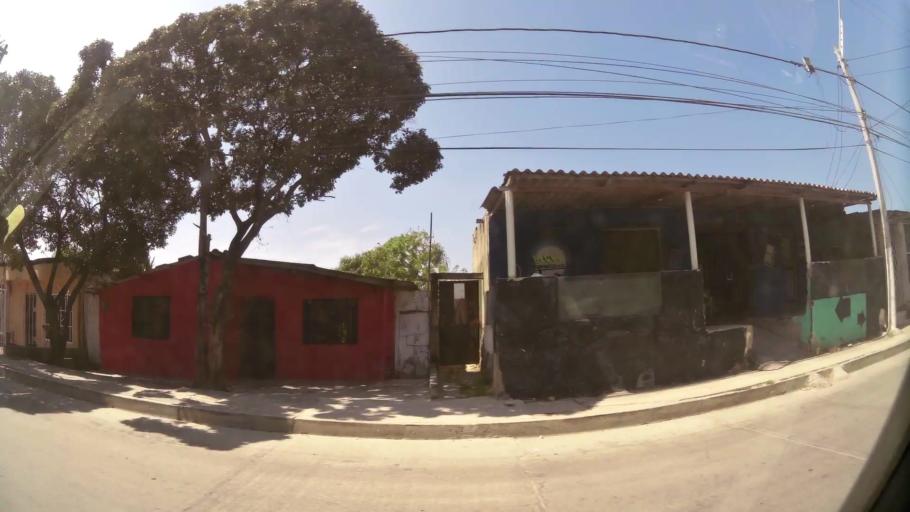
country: CO
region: Atlantico
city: Barranquilla
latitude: 10.9754
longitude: -74.8247
